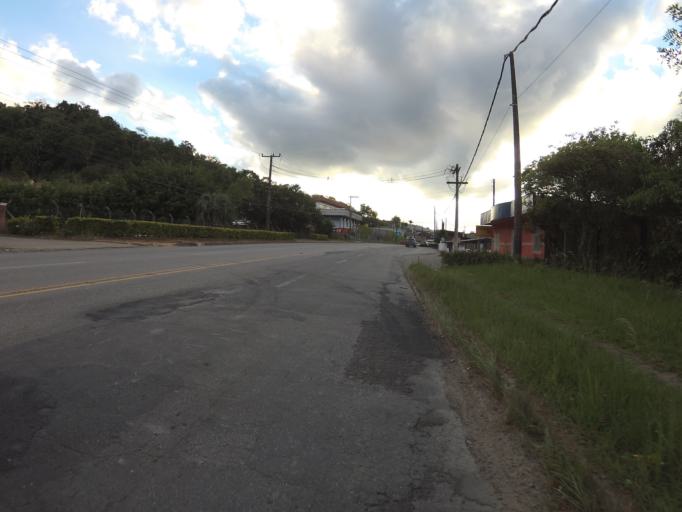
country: BR
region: Santa Catarina
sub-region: Blumenau
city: Blumenau
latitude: -26.8929
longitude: -49.1244
